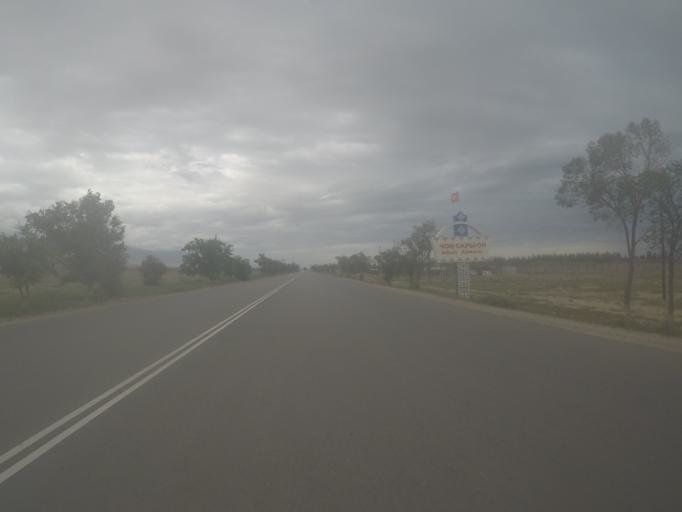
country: KG
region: Ysyk-Koel
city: Cholpon-Ata
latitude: 42.5811
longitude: 76.7168
